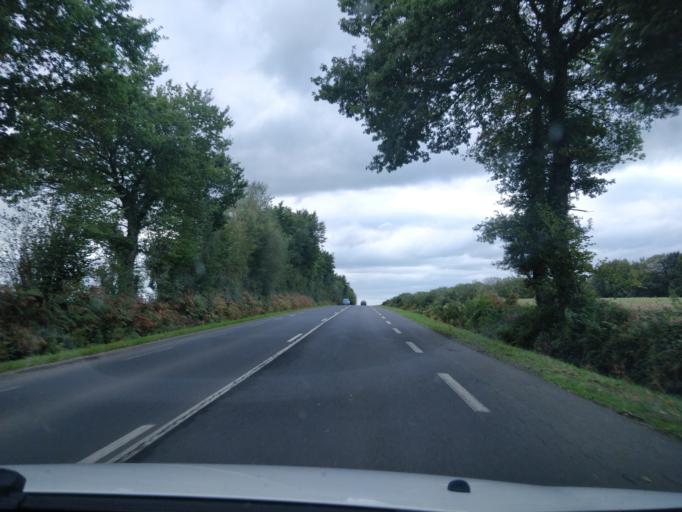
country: FR
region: Lower Normandy
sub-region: Departement du Calvados
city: Saint-Sever-Calvados
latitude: 48.8227
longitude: -1.1307
